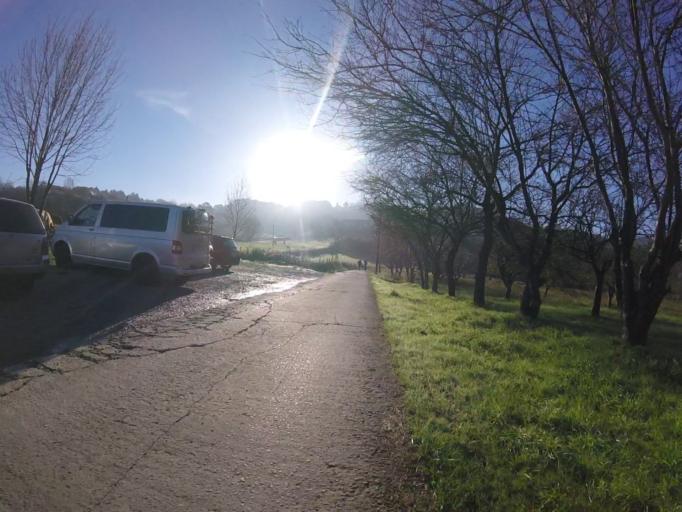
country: ES
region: Basque Country
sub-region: Provincia de Guipuzcoa
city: Lasarte
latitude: 43.2686
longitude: -2.0349
